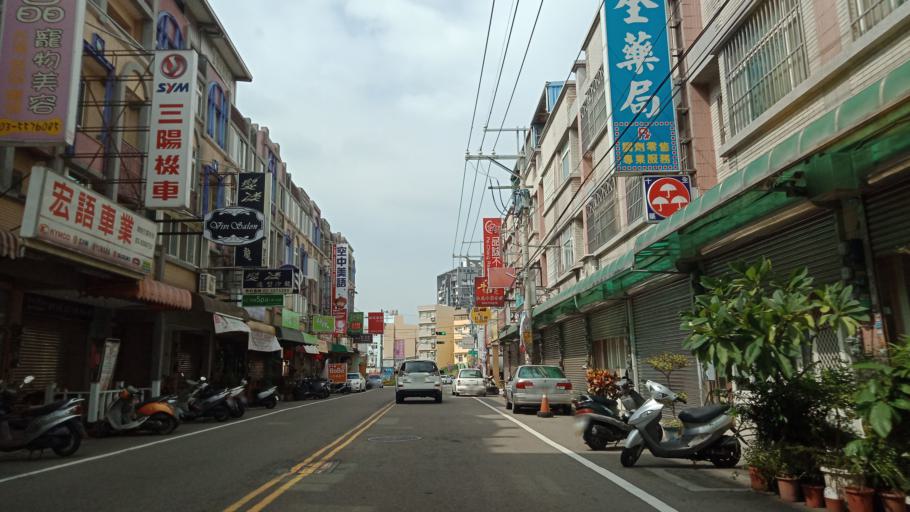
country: TW
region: Taiwan
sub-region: Hsinchu
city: Zhubei
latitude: 24.8705
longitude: 120.9938
